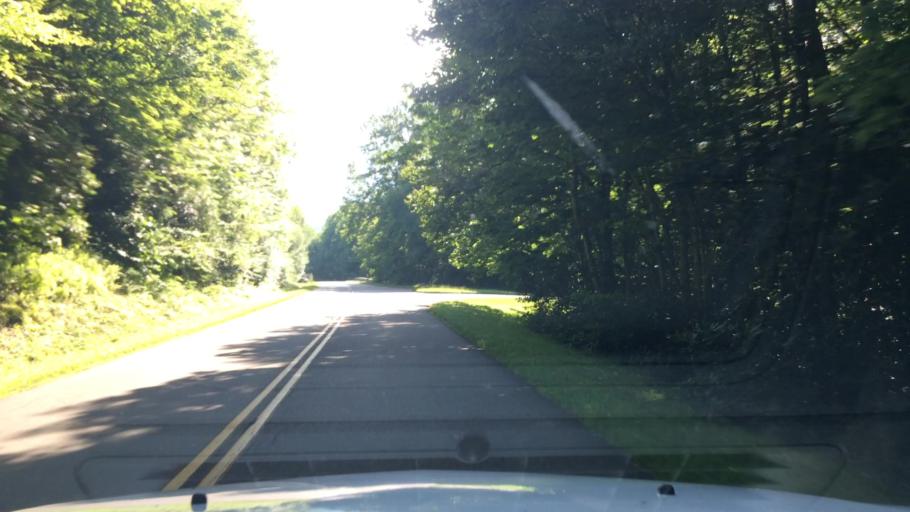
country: US
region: North Carolina
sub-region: Watauga County
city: Foscoe
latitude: 36.1316
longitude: -81.7605
